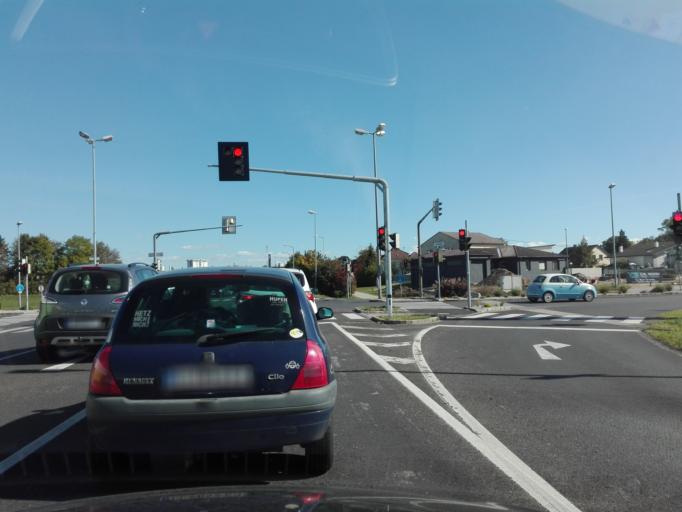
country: AT
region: Upper Austria
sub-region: Politischer Bezirk Linz-Land
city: Enns
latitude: 48.2158
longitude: 14.4649
